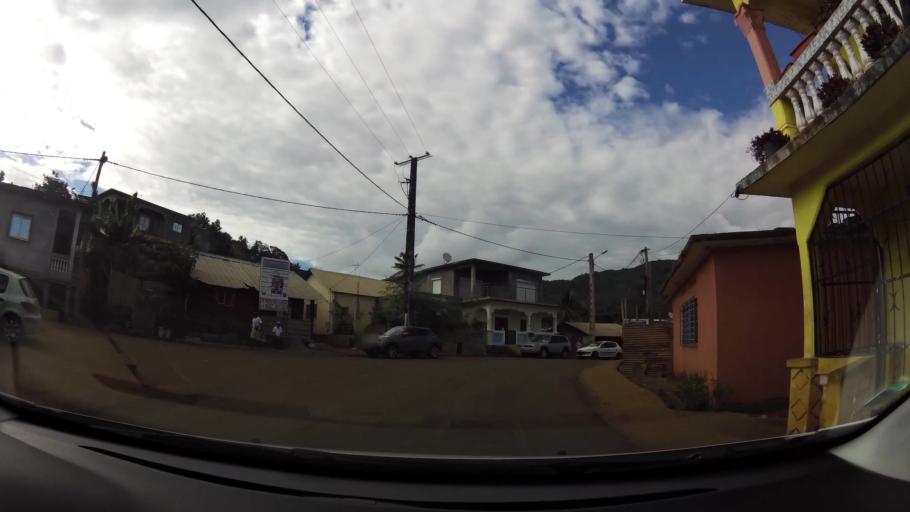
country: YT
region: Ouangani
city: Ouangani
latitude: -12.8476
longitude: 45.1378
